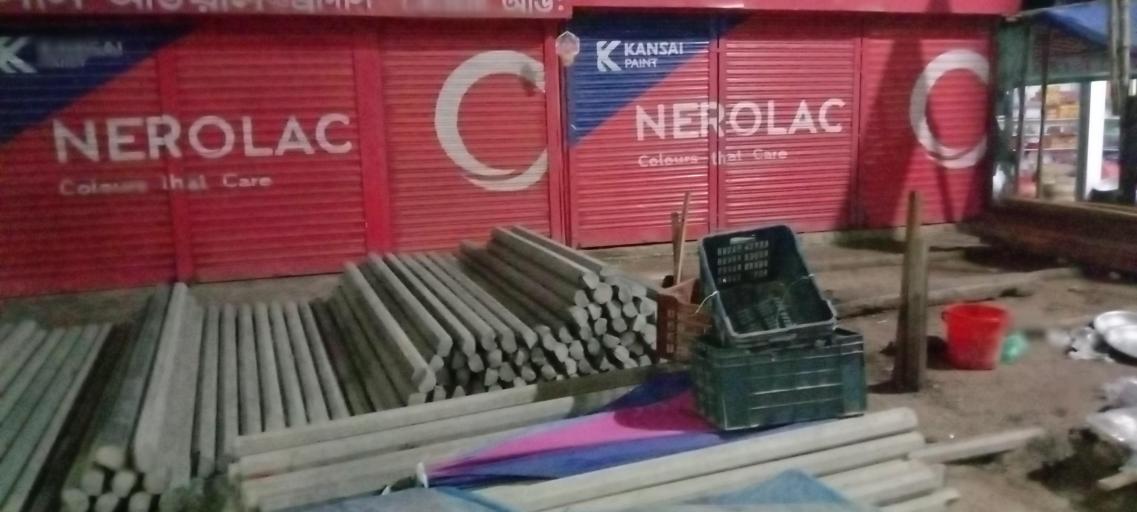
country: BD
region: Dhaka
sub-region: Dhaka
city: Dhaka
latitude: 23.6604
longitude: 90.3606
